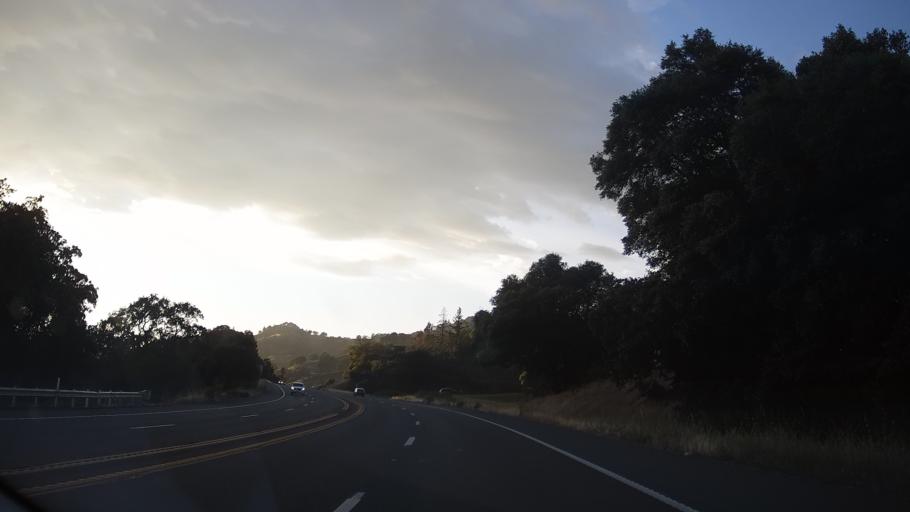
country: US
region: California
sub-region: Mendocino County
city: Redwood Valley
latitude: 39.2823
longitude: -123.2592
